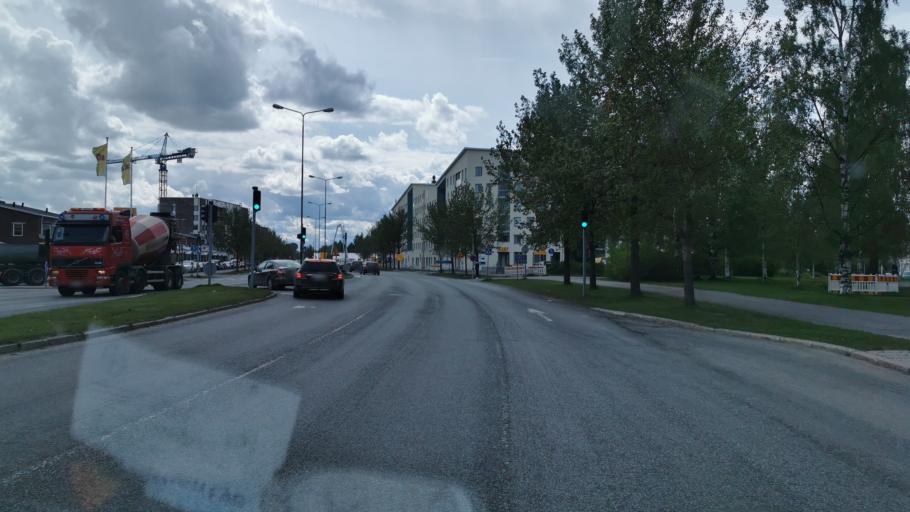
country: FI
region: Northern Ostrobothnia
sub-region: Oulu
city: Oulu
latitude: 65.0035
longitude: 25.4634
